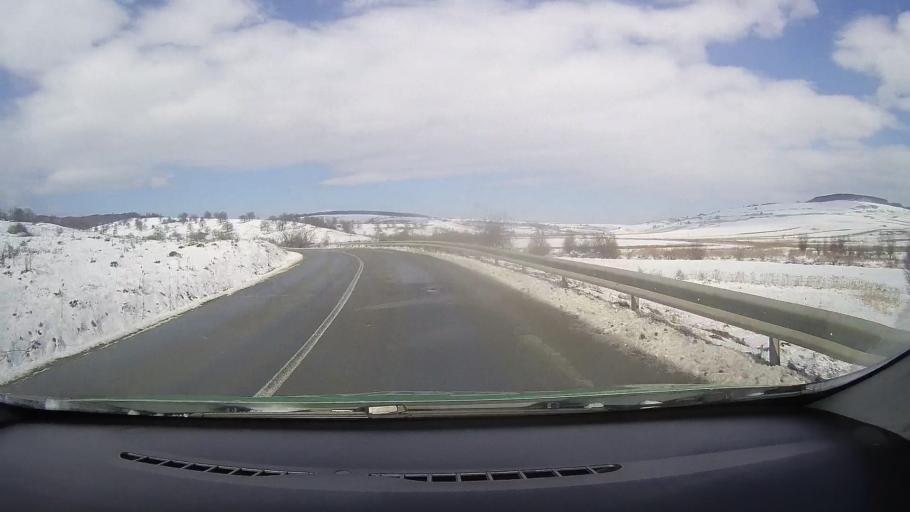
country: RO
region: Sibiu
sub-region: Comuna Altina
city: Altina
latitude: 45.9418
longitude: 24.4540
